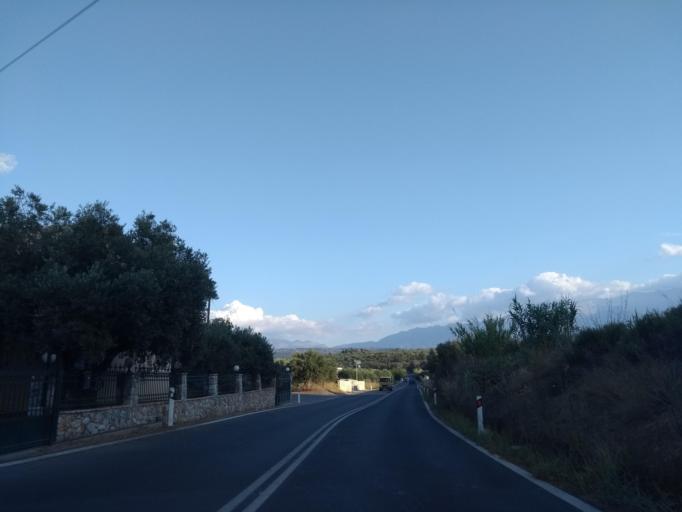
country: GR
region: Crete
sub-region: Nomos Chanias
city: Kalivai
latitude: 35.4642
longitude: 24.1533
